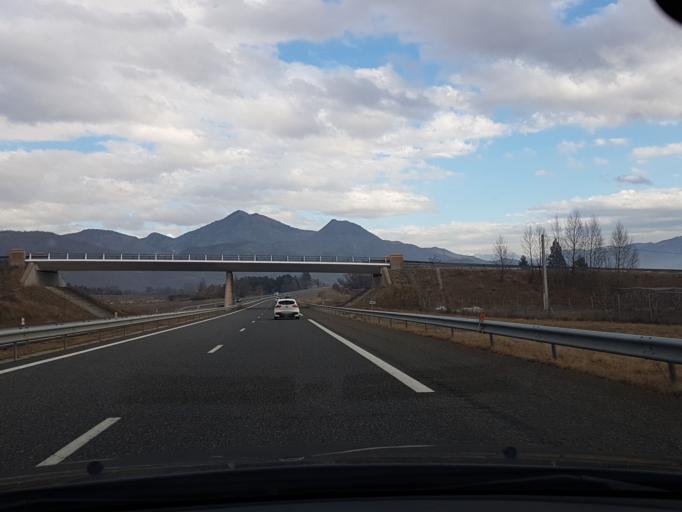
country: FR
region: Provence-Alpes-Cote d'Azur
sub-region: Departement des Hautes-Alpes
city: Tallard
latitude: 44.4051
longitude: 5.9556
